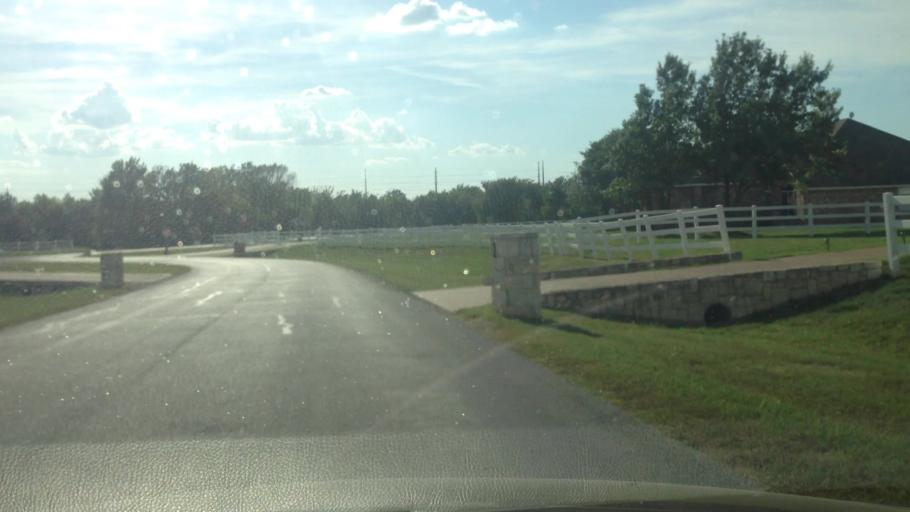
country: US
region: Texas
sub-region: Tarrant County
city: Haslet
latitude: 32.9228
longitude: -97.3822
